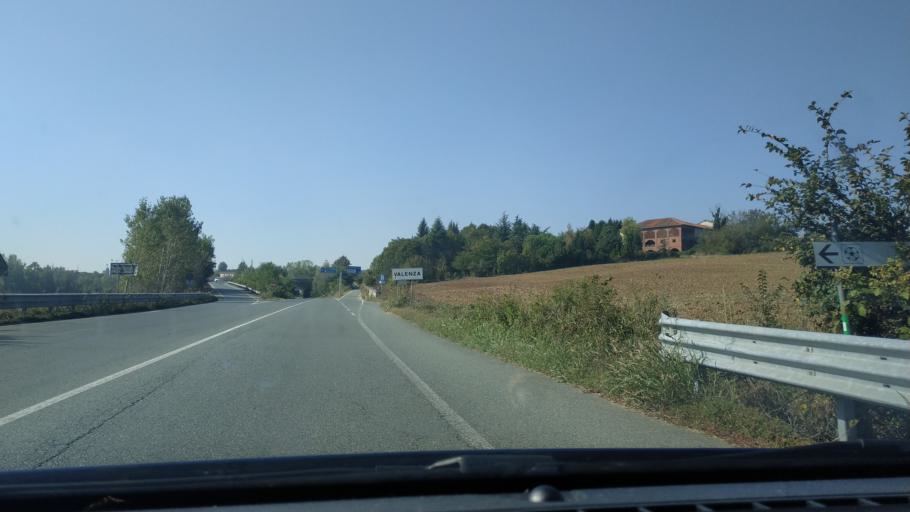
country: IT
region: Piedmont
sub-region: Provincia di Alessandria
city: Valenza
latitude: 45.0272
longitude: 8.6313
